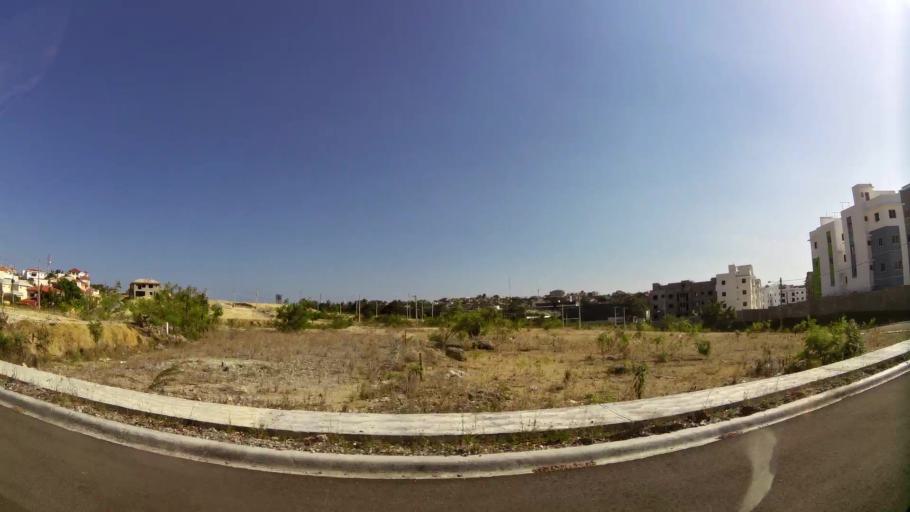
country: DO
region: Nacional
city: Santo Domingo
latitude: 18.4634
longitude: -69.9864
